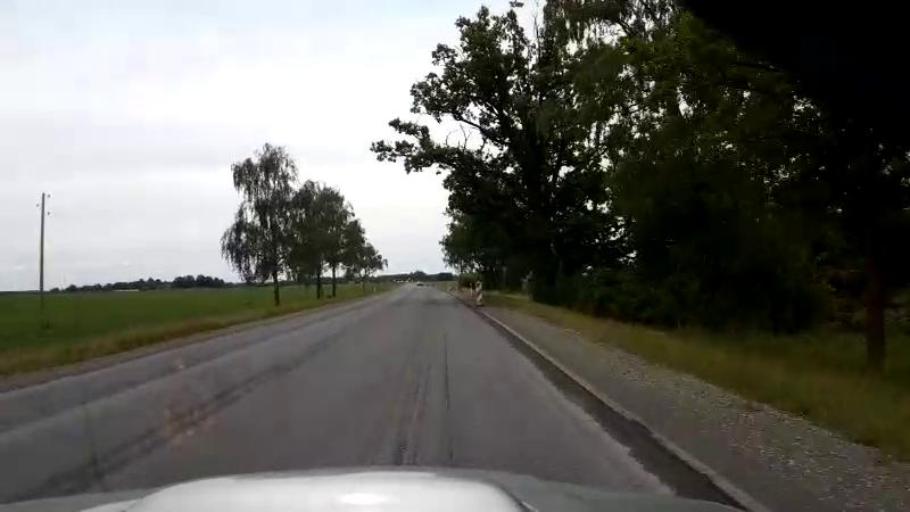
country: LV
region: Bauskas Rajons
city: Bauska
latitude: 56.3392
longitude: 24.2938
